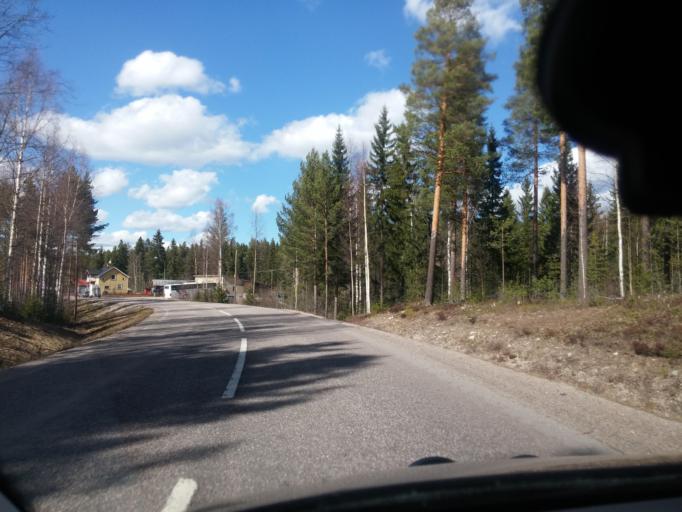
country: SE
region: Gaevleborg
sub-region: Ovanakers Kommun
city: Edsbyn
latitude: 61.2512
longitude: 15.8932
